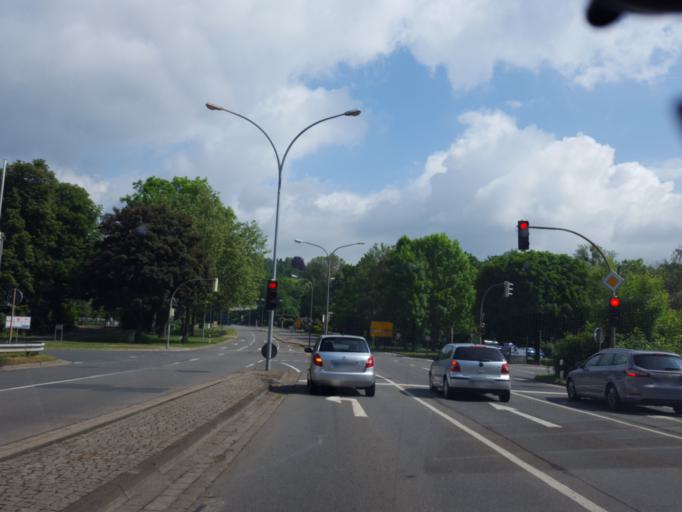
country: DE
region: Lower Saxony
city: Osterode am Harz
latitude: 51.7257
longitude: 10.2613
